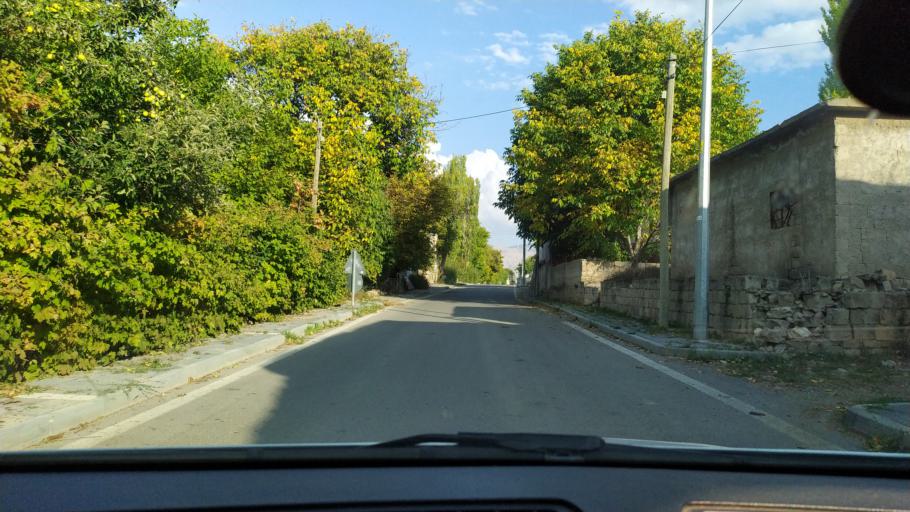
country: TR
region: Kayseri
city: Akkisla
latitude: 38.9998
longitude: 36.1647
